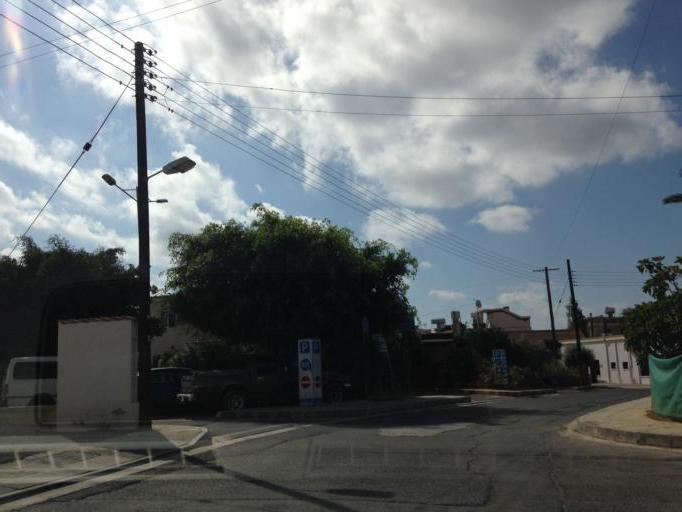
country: CY
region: Pafos
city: Chlorakas
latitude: 34.7987
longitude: 32.4089
